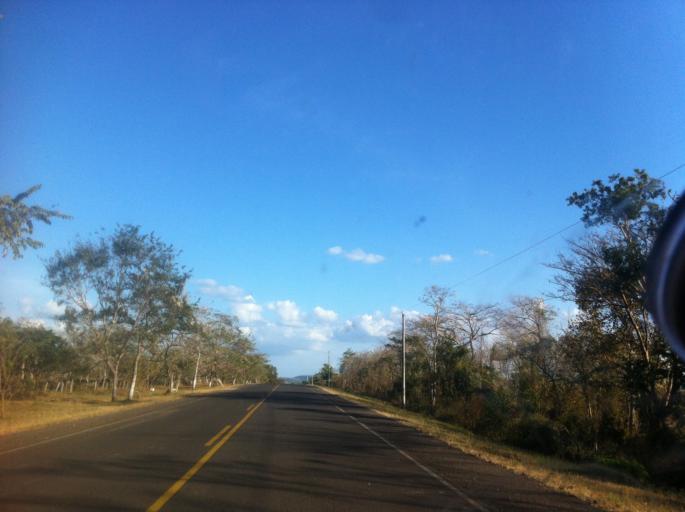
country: NI
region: Rio San Juan
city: Morrito
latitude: 11.7414
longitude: -84.9862
